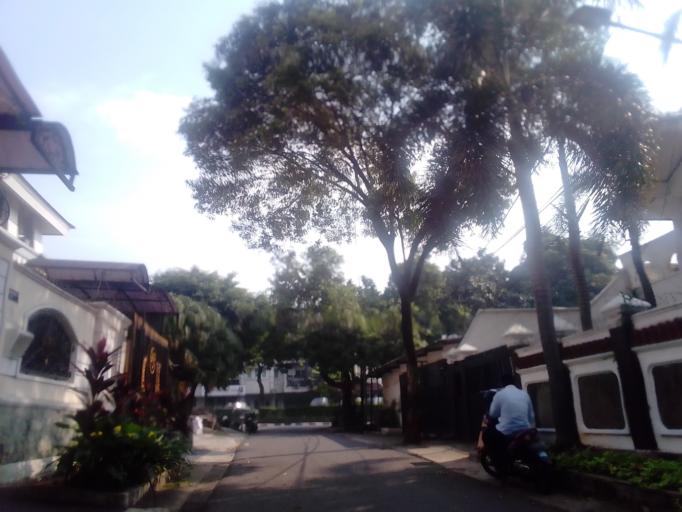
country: ID
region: Jakarta Raya
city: Jakarta
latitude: -6.2553
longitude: 106.7999
